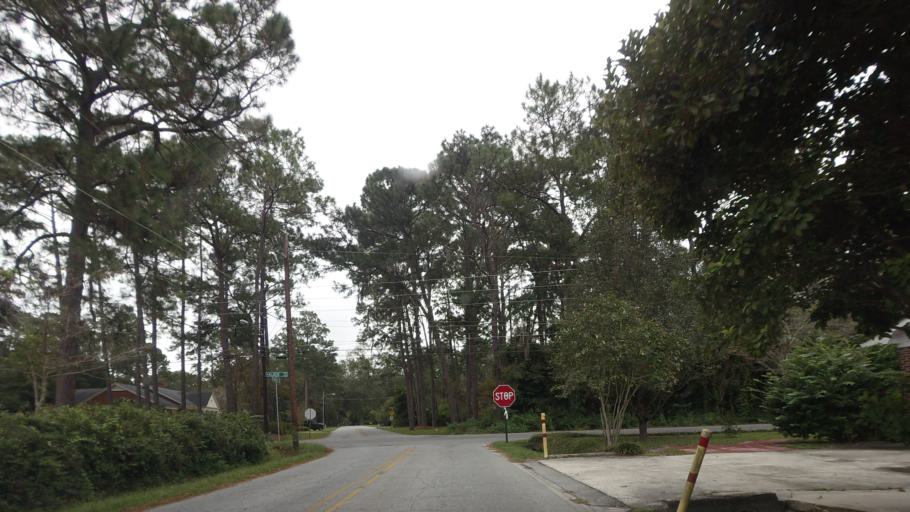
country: US
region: Georgia
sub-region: Lowndes County
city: Remerton
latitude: 30.8532
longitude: -83.2957
